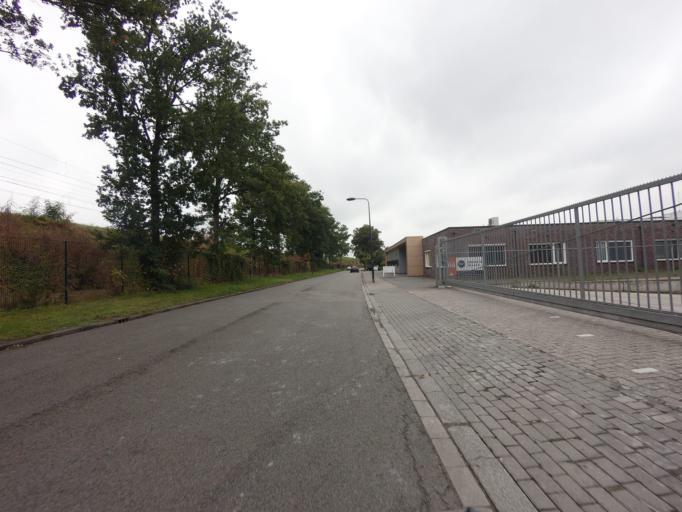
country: NL
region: Overijssel
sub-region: Gemeente Enschede
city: Enschede
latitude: 52.2213
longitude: 6.8746
